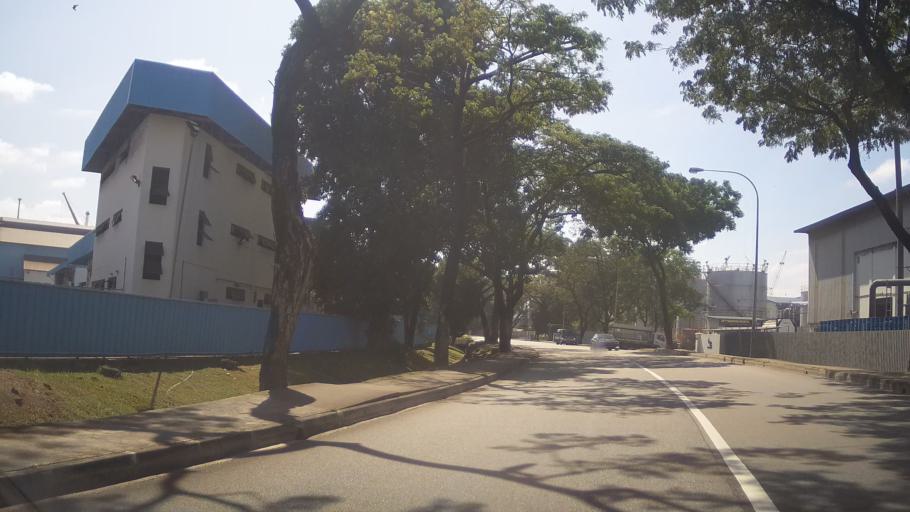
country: SG
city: Singapore
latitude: 1.3067
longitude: 103.6995
